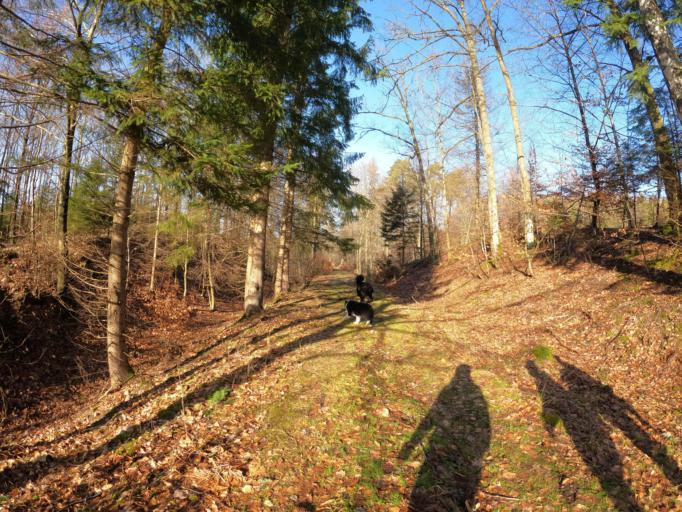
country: PL
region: West Pomeranian Voivodeship
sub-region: Powiat koszalinski
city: Polanow
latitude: 54.2054
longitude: 16.7214
